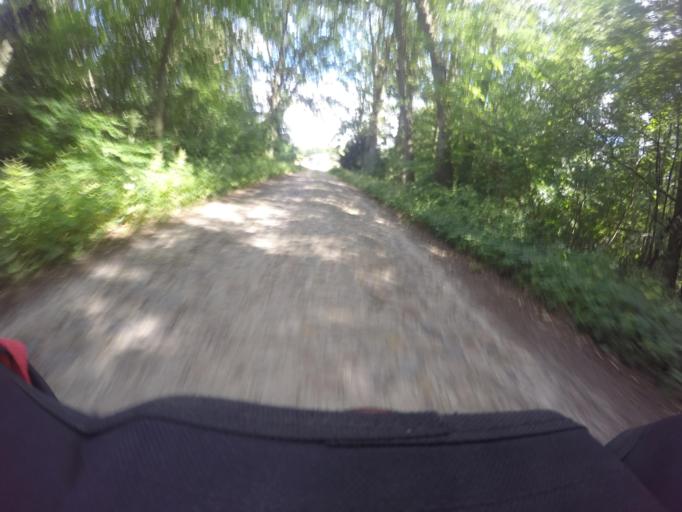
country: DE
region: Lower Saxony
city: Thomasburg
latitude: 53.2233
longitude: 10.6722
